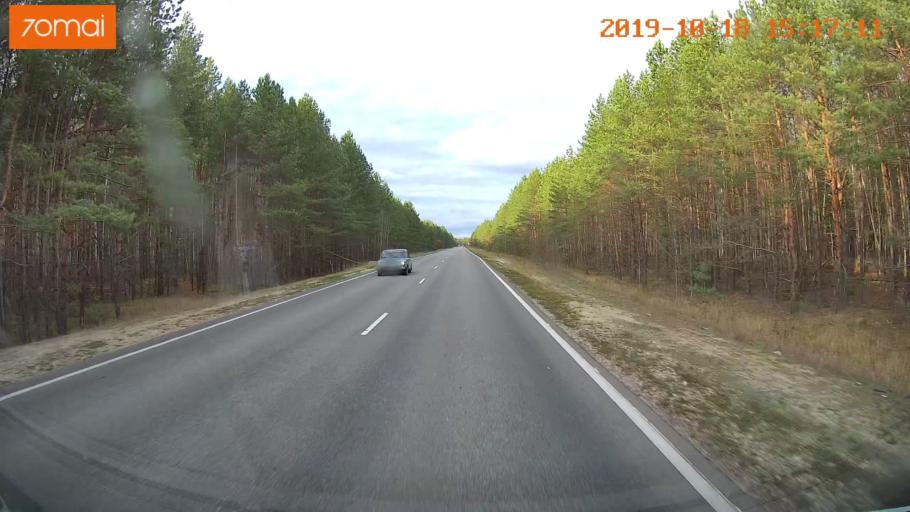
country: RU
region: Vladimir
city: Anopino
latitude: 55.6458
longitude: 40.7260
